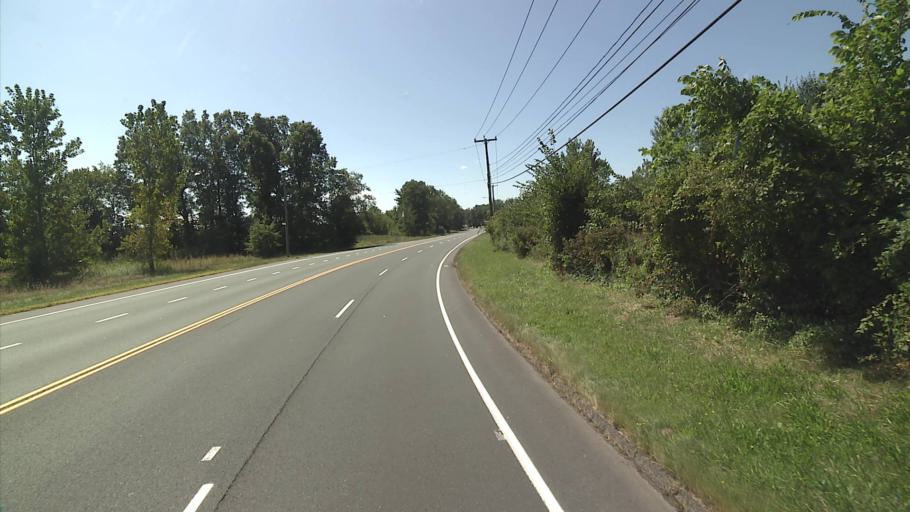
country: US
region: Connecticut
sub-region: Hartford County
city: West Hartford
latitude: 41.8092
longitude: -72.7490
